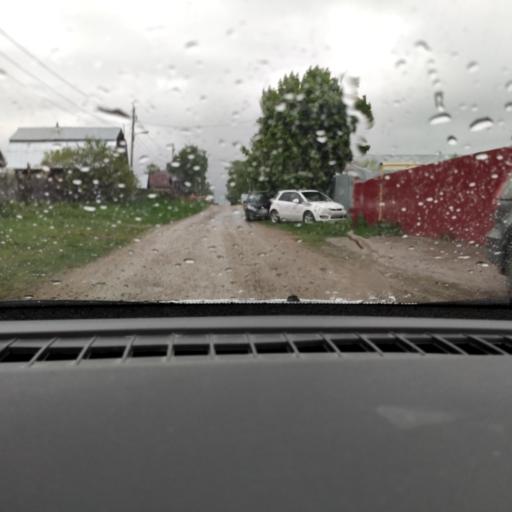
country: RU
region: Perm
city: Kondratovo
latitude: 58.0515
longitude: 56.0241
